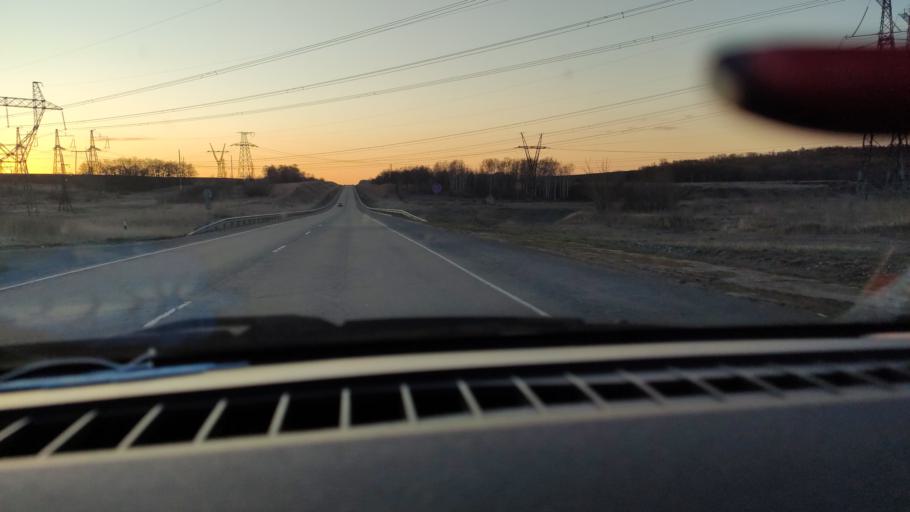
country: RU
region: Saratov
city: Yelshanka
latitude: 51.8230
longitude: 46.3177
